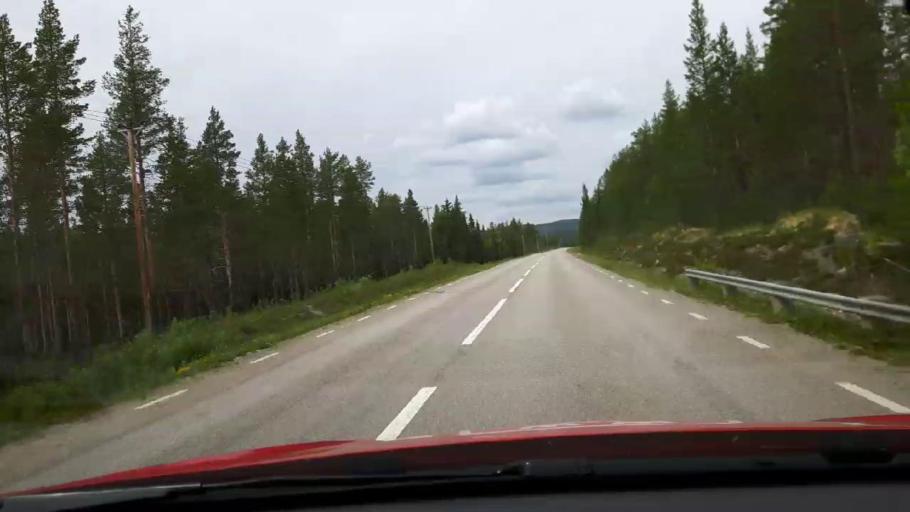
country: SE
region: Jaemtland
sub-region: Harjedalens Kommun
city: Sveg
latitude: 62.3976
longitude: 13.7476
